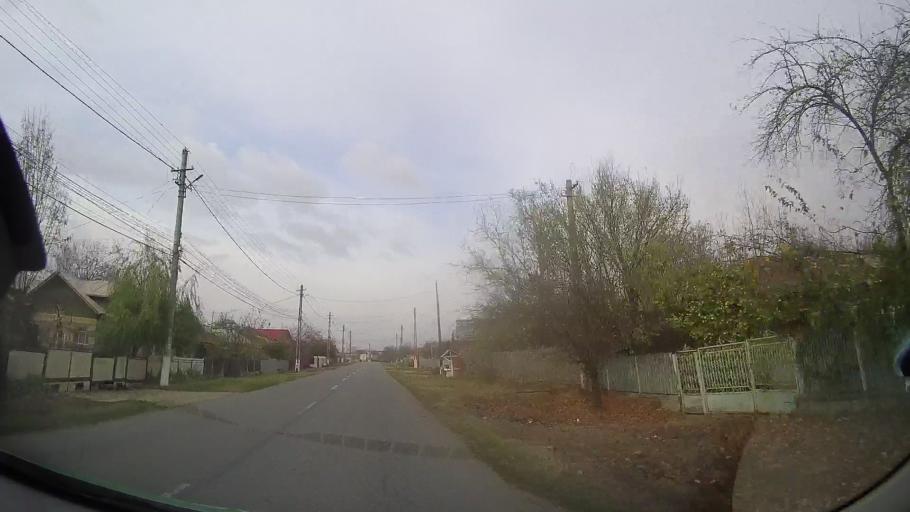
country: RO
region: Prahova
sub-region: Comuna Gorgota
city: Potigrafu
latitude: 44.7801
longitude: 26.1030
